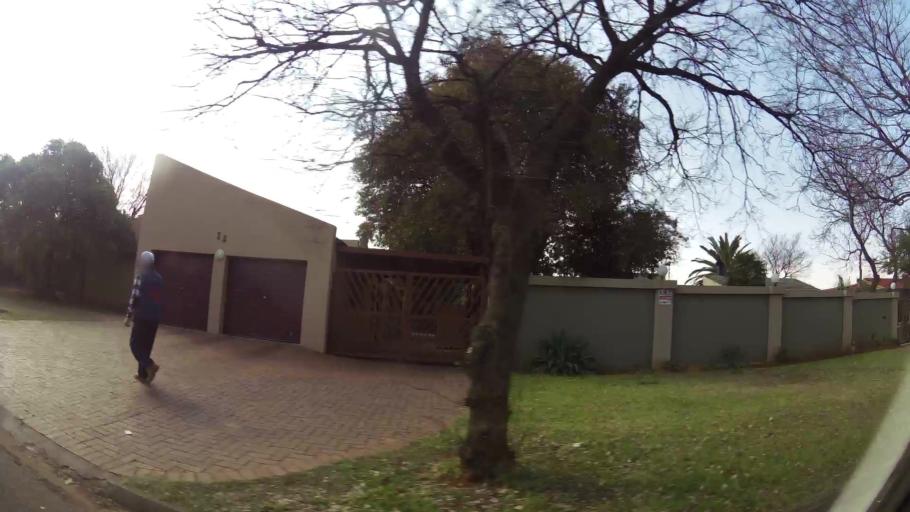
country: ZA
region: Gauteng
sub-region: Ekurhuleni Metropolitan Municipality
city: Boksburg
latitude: -26.1909
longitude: 28.2359
